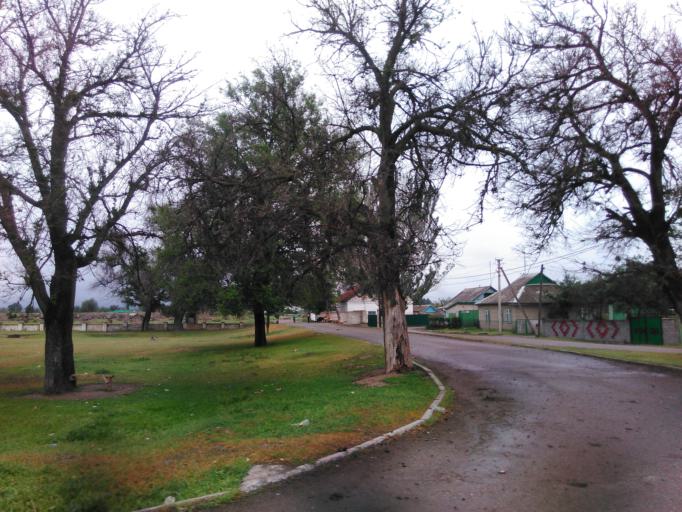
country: KG
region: Chuy
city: Tokmok
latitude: 42.8145
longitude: 75.3251
